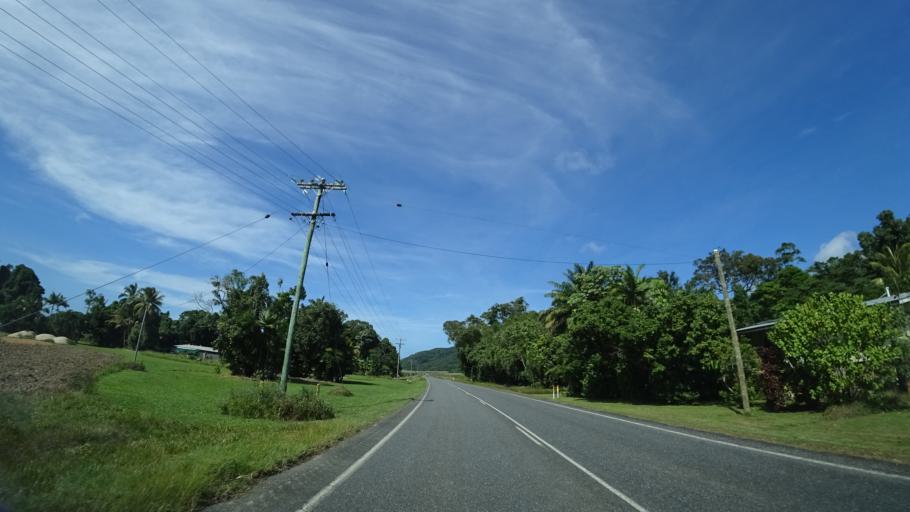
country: AU
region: Queensland
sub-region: Cairns
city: Port Douglas
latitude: -16.3051
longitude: 145.3904
